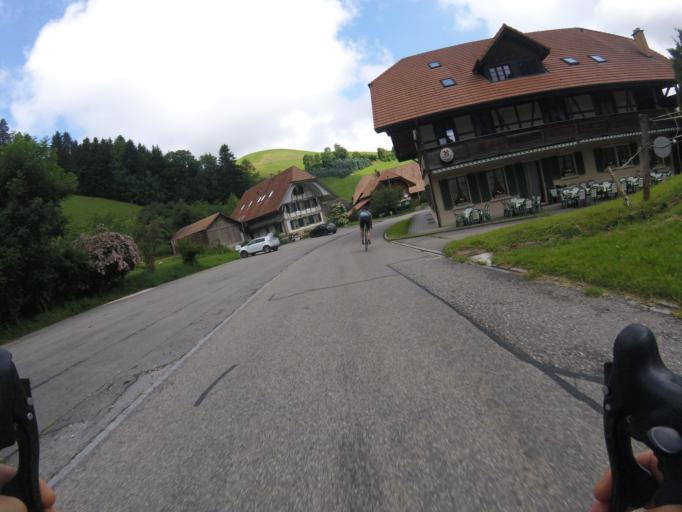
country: CH
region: Bern
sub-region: Emmental District
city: Krauchthal
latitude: 46.9894
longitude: 7.5812
